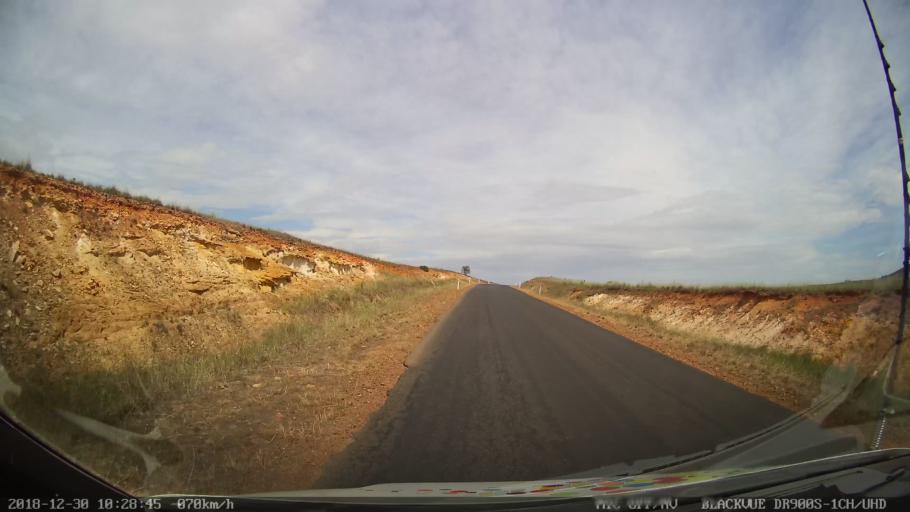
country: AU
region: New South Wales
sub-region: Snowy River
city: Berridale
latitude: -36.5046
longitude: 148.9177
